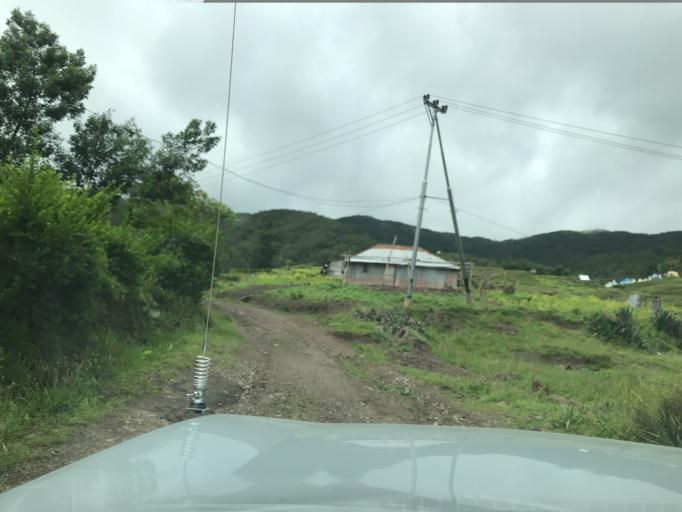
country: TL
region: Ainaro
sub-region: Ainaro
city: Ainaro
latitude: -8.8652
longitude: 125.5549
